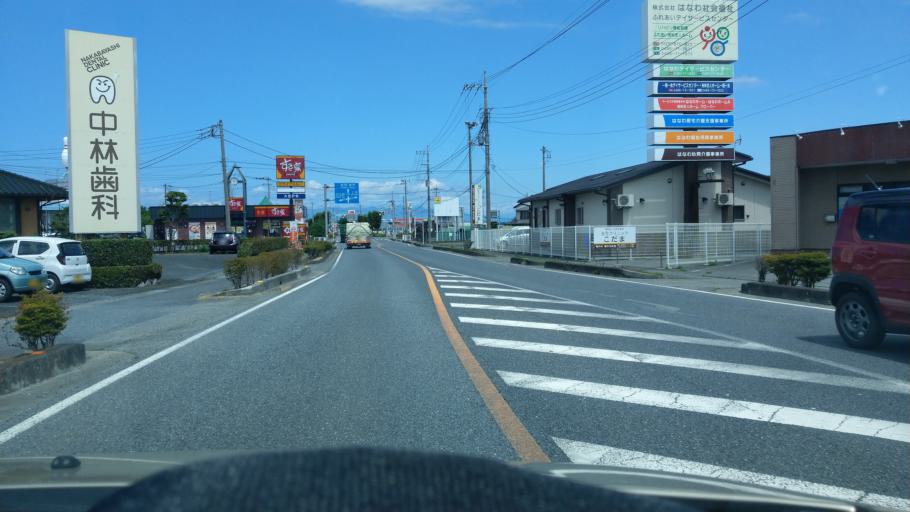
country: JP
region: Saitama
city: Kodamacho-kodamaminami
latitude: 36.1990
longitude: 139.1328
